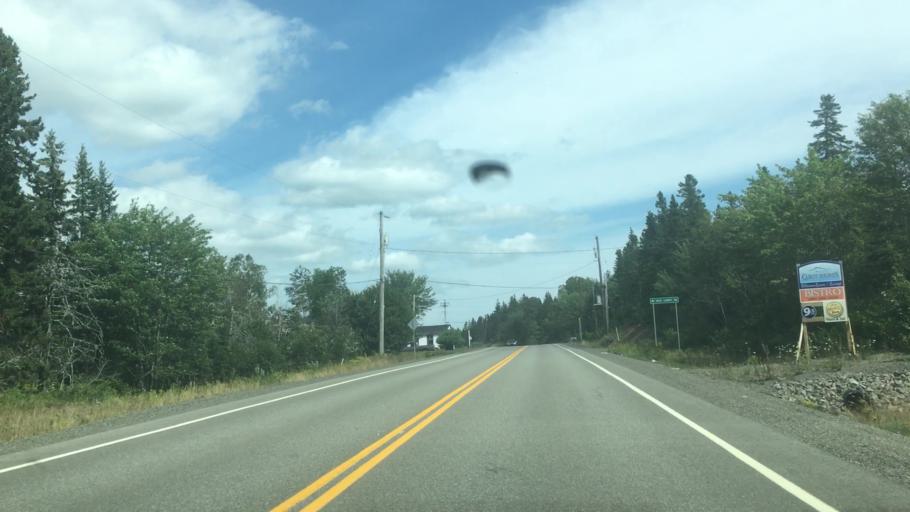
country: CA
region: Nova Scotia
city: Sydney Mines
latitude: 46.3275
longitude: -60.6050
